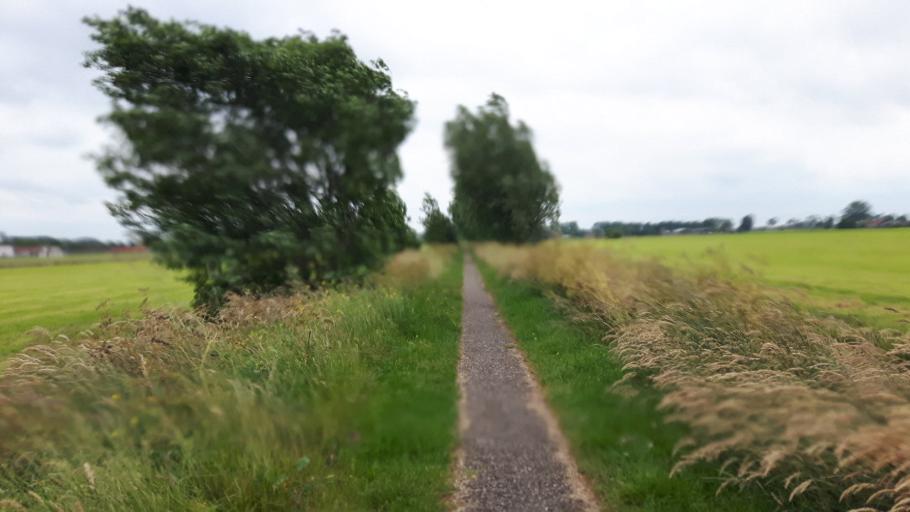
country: NL
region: Utrecht
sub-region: Gemeente Oudewater
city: Oudewater
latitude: 52.0299
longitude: 4.8515
